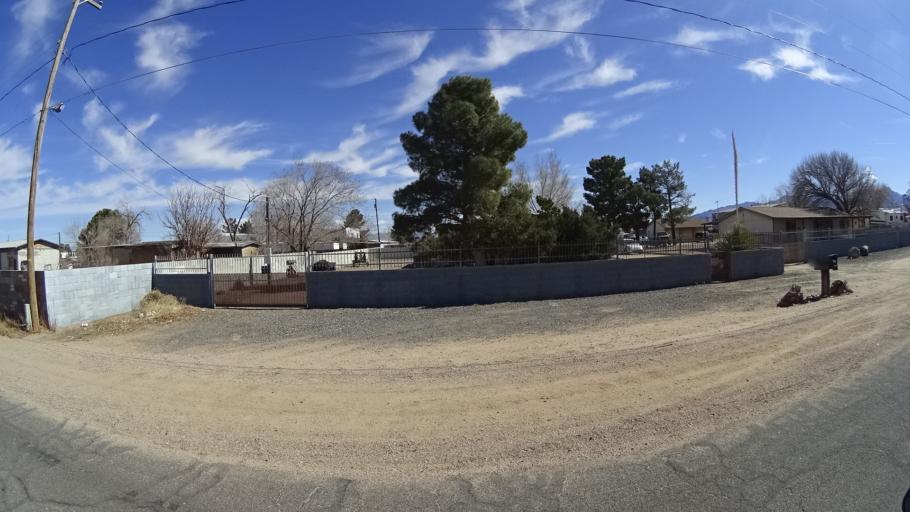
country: US
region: Arizona
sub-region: Mohave County
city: New Kingman-Butler
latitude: 35.2421
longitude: -114.0133
